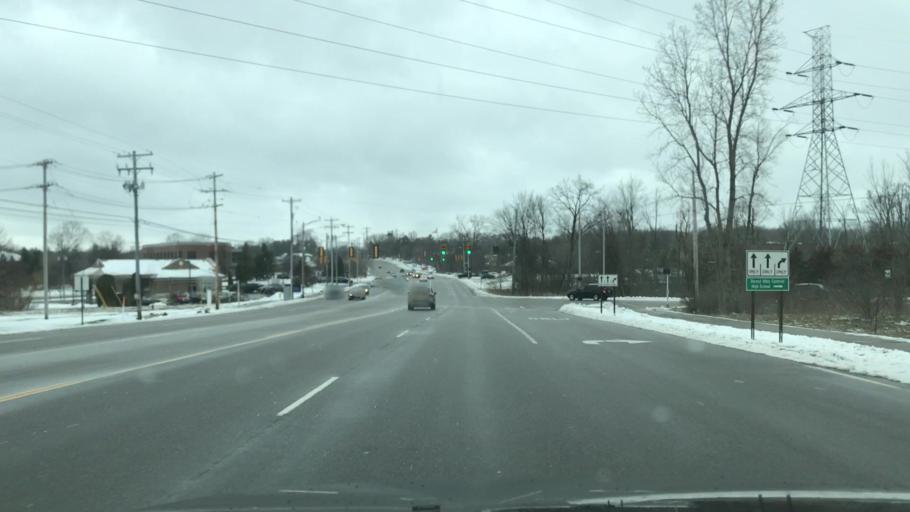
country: US
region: Michigan
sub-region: Kent County
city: Forest Hills
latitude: 42.9408
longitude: -85.5378
